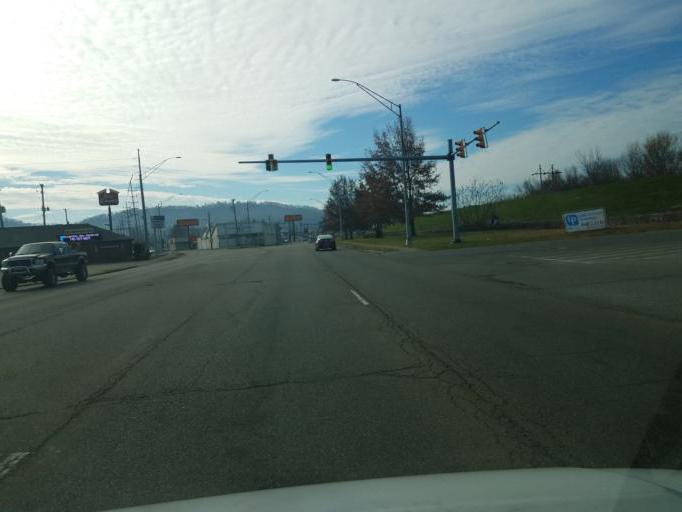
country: US
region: Ohio
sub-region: Scioto County
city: Portsmouth
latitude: 38.7430
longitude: -82.9939
